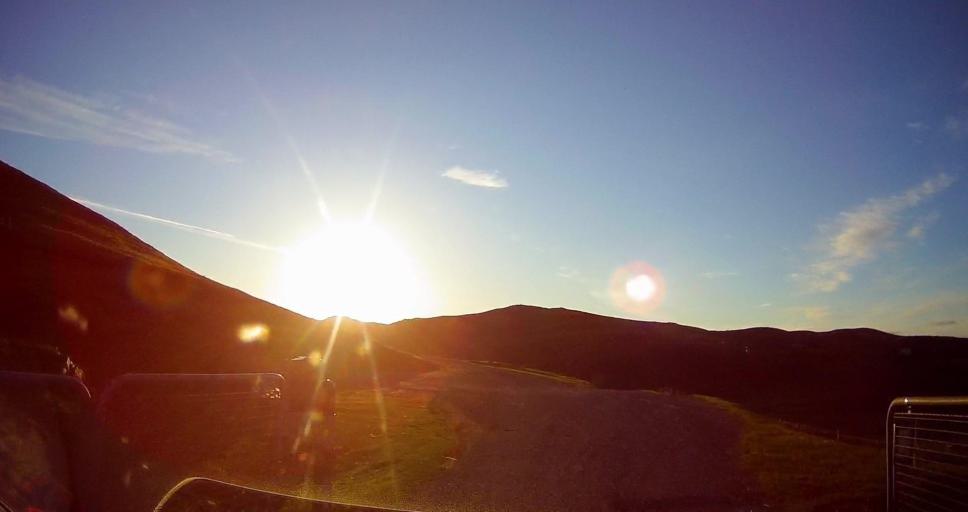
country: GB
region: Scotland
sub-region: Shetland Islands
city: Lerwick
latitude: 60.4481
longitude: -1.4161
